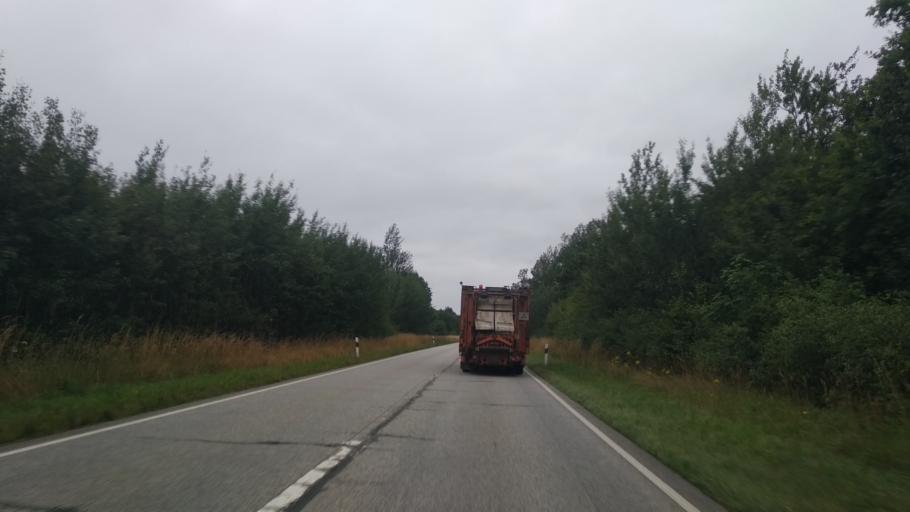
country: DE
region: Schleswig-Holstein
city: Lurschau
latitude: 54.5729
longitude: 9.4797
